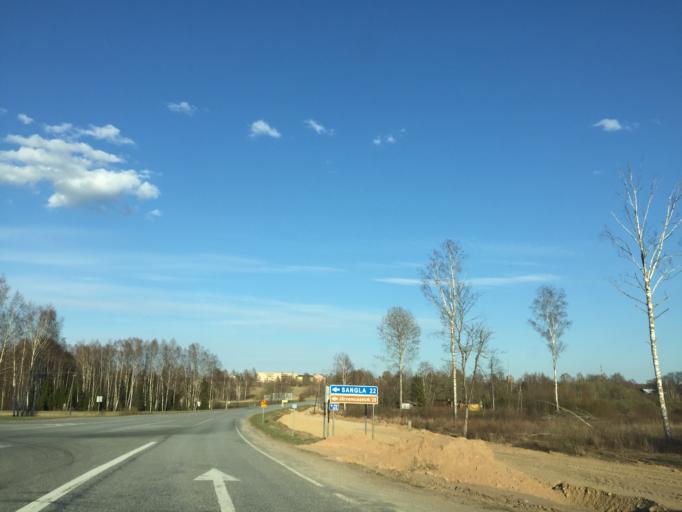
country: EE
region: Tartu
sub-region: Elva linn
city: Elva
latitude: 58.1462
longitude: 26.2306
